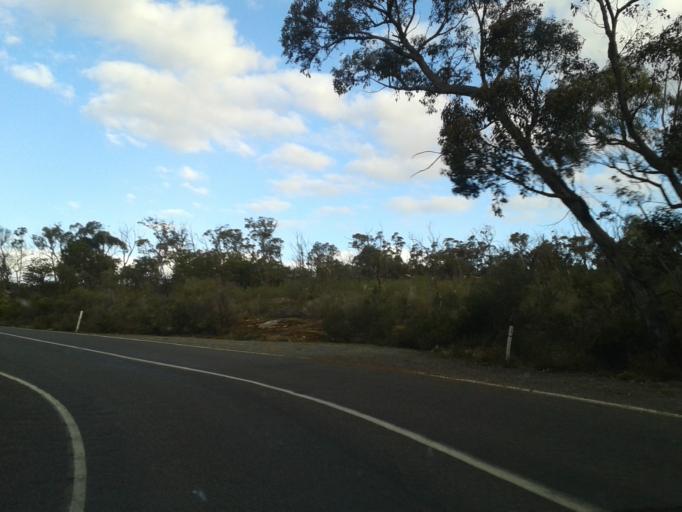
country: AU
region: Victoria
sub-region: Northern Grampians
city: Stawell
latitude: -37.1408
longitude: 142.4382
